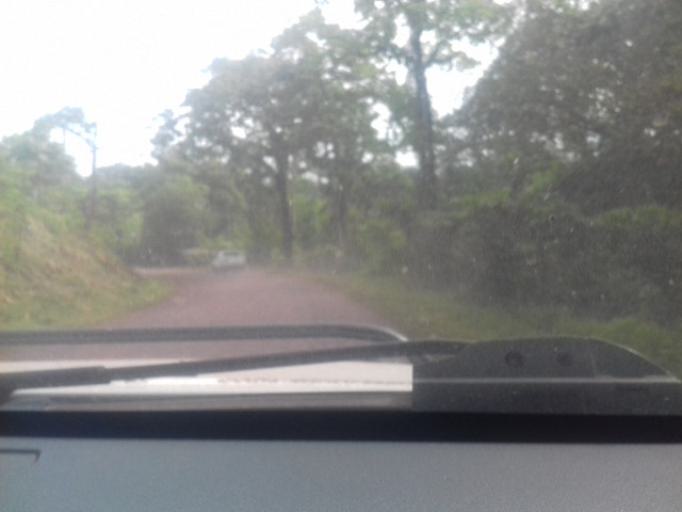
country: NI
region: Atlantico Norte (RAAN)
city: Waslala
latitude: 13.4329
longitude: -85.3110
